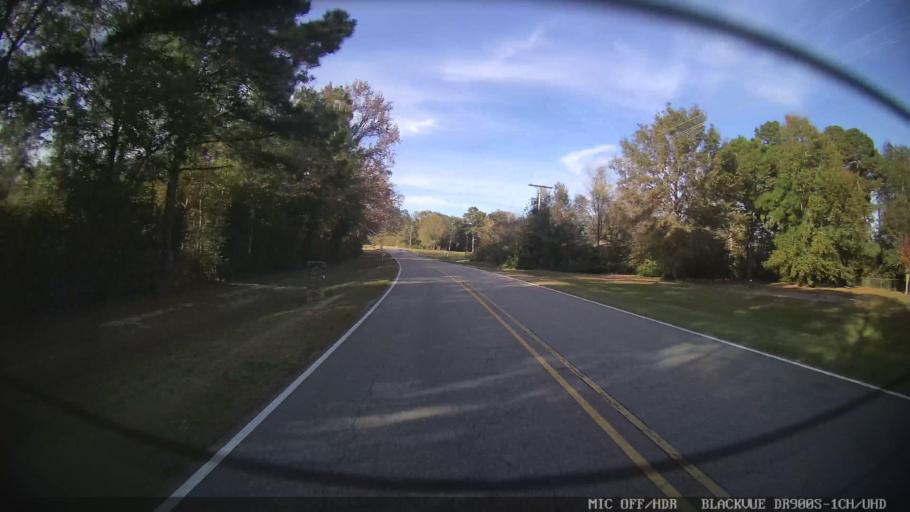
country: US
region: Mississippi
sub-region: Lamar County
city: Purvis
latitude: 31.1921
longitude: -89.2876
